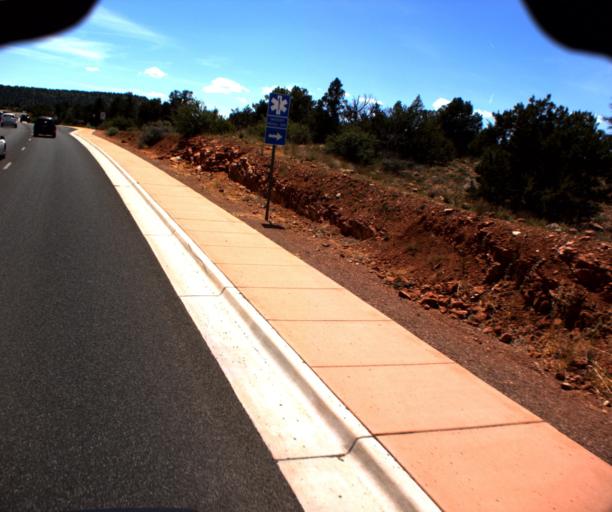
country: US
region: Arizona
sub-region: Yavapai County
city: West Sedona
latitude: 34.8579
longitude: -111.8211
